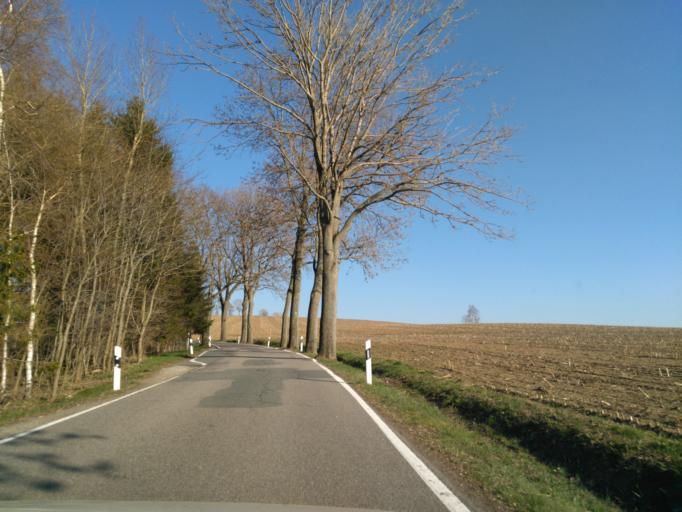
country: DE
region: Saxony
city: Schlettau
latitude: 50.5429
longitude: 12.9723
